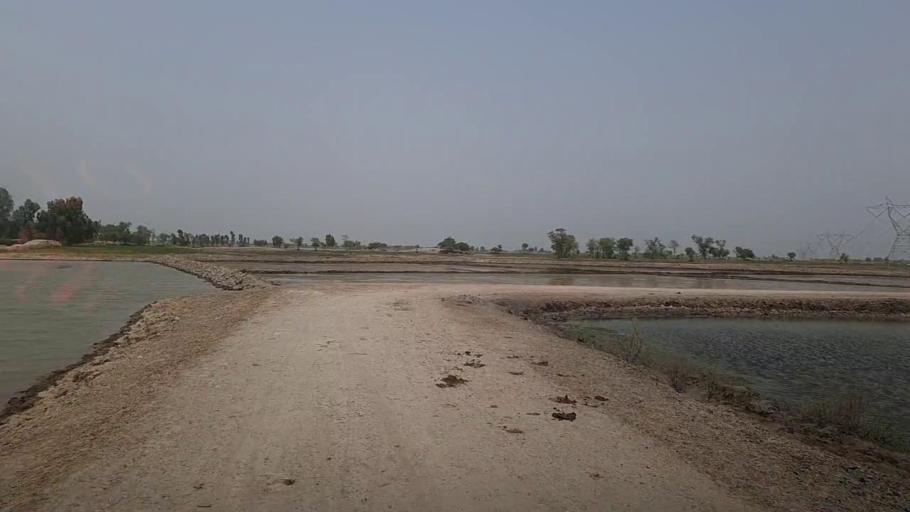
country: PK
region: Sindh
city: Sita Road
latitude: 27.0699
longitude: 67.8473
